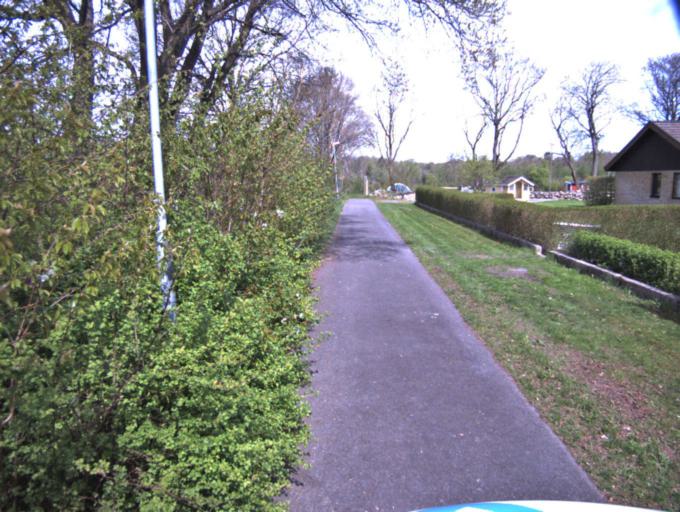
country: SE
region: Skane
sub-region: Kristianstads Kommun
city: Onnestad
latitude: 55.9977
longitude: 14.0347
